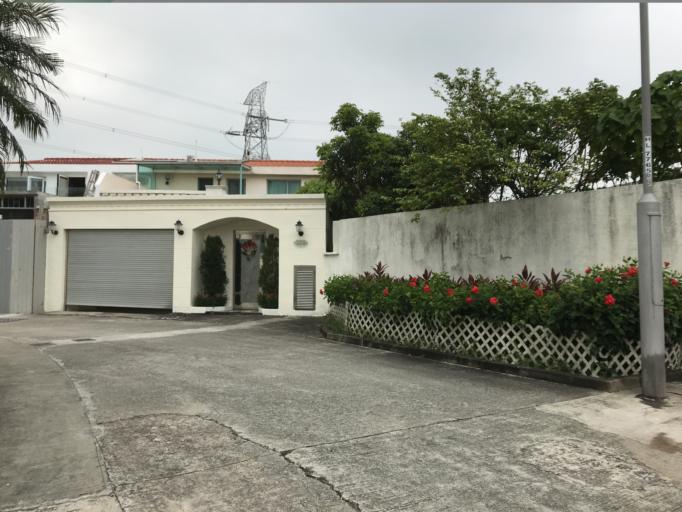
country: HK
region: Tai Po
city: Tai Po
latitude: 22.4660
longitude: 114.1529
